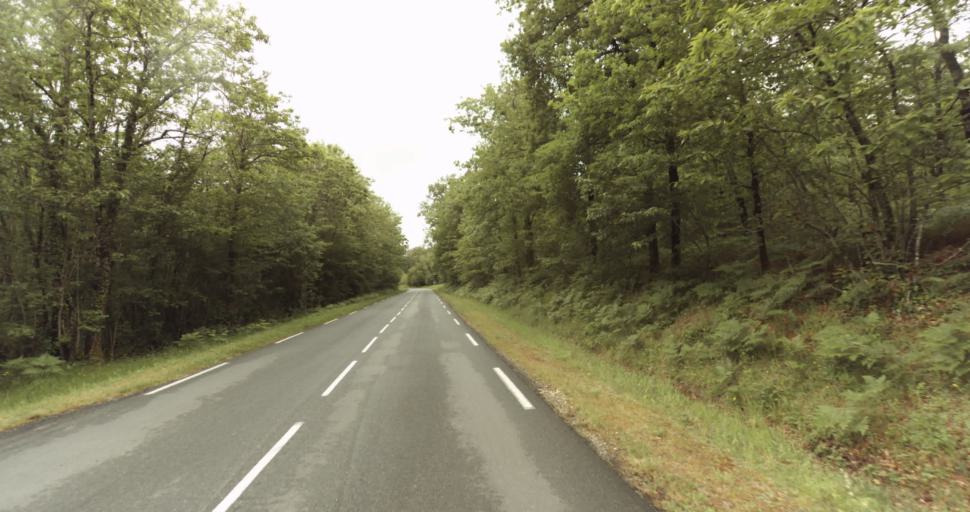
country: FR
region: Aquitaine
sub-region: Departement de la Dordogne
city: Belves
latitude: 44.6688
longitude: 1.0036
